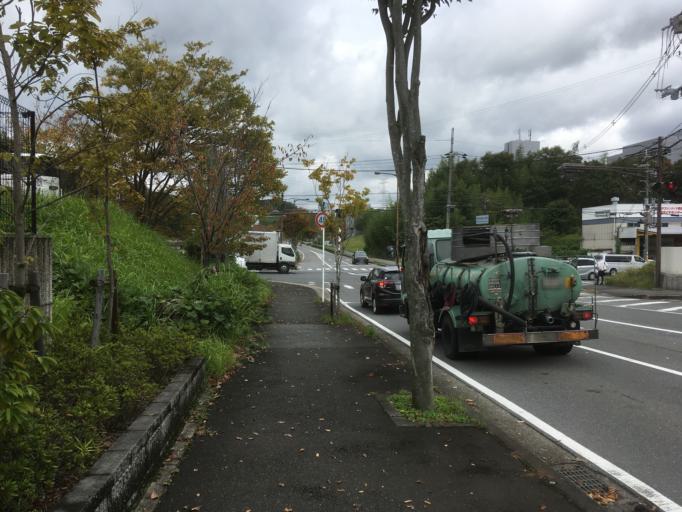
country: JP
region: Nara
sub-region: Ikoma-shi
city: Ikoma
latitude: 34.7295
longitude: 135.7311
